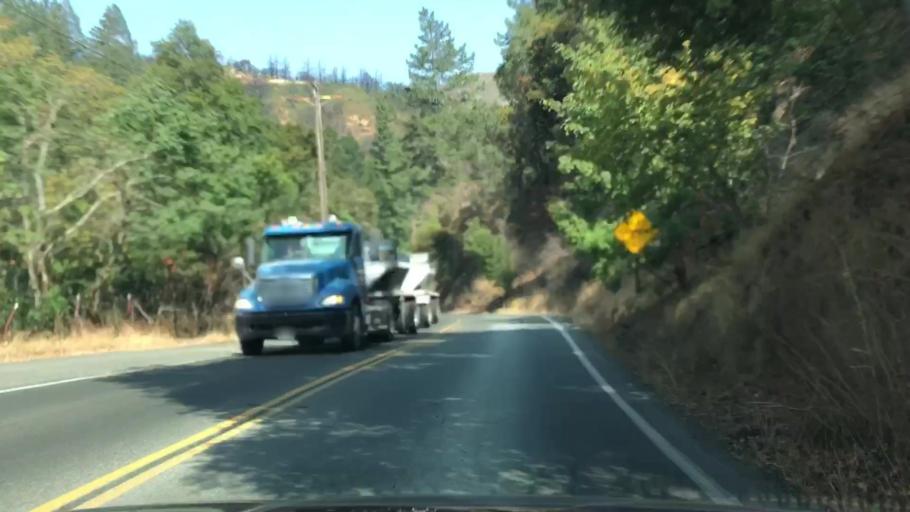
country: US
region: California
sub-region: Napa County
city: Calistoga
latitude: 38.5537
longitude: -122.6623
